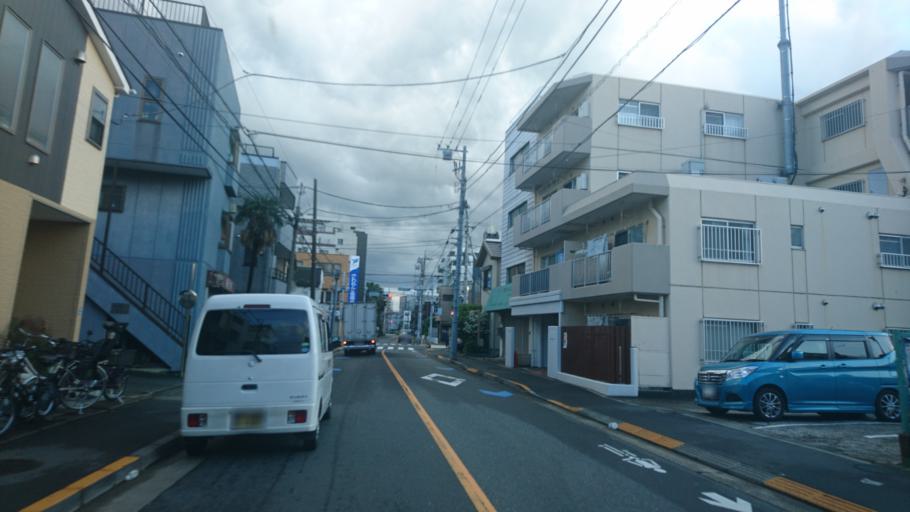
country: JP
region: Kanagawa
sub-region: Kawasaki-shi
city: Kawasaki
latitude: 35.5577
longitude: 139.7425
